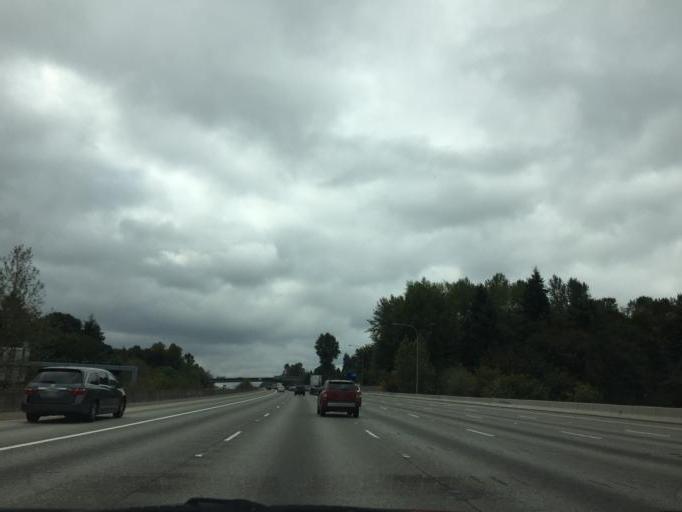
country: US
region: Washington
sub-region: King County
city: SeaTac
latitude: 47.4483
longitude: -122.2667
